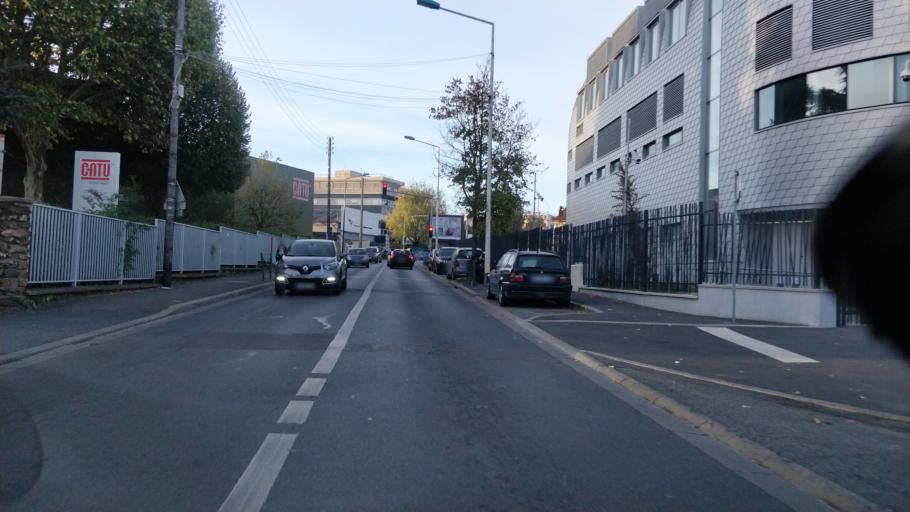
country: FR
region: Ile-de-France
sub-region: Departement des Hauts-de-Seine
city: Bagneux
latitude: 48.8009
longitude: 2.3019
